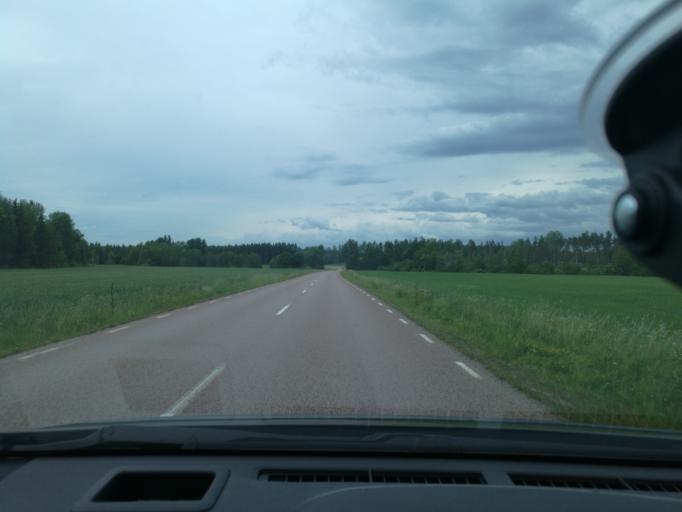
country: SE
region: Vaestmanland
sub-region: Vasteras
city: Skultuna
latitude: 59.7429
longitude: 16.4114
